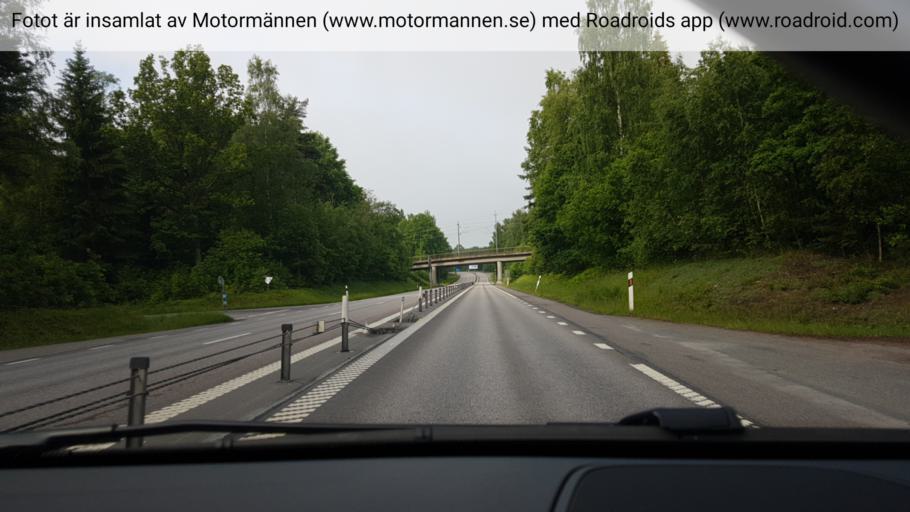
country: SE
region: OEstergoetland
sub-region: Motala Kommun
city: Motala
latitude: 58.5716
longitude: 15.0760
